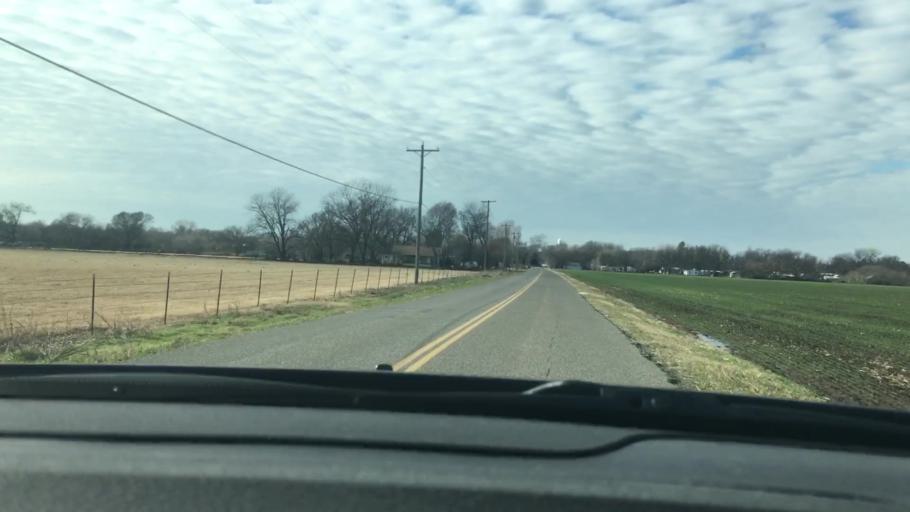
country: US
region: Oklahoma
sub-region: Garvin County
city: Pauls Valley
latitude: 34.7388
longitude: -97.2022
